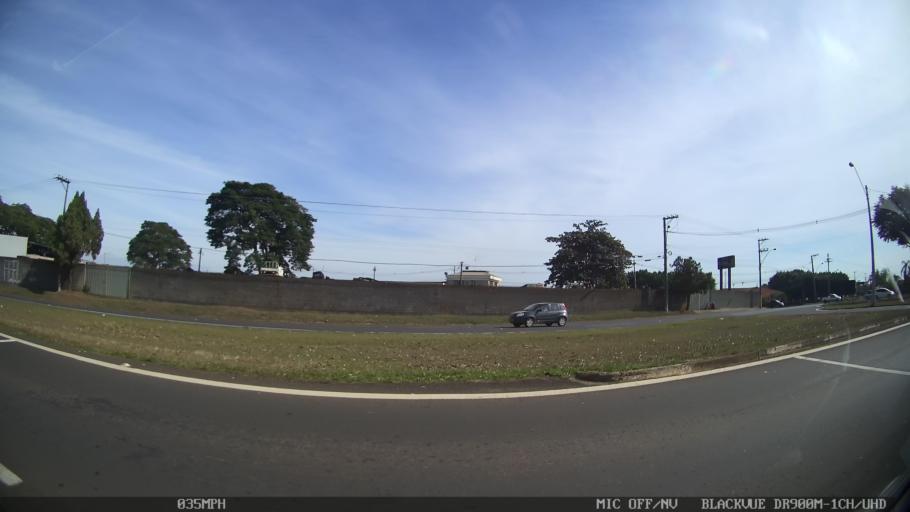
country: BR
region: Sao Paulo
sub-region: Piracicaba
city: Piracicaba
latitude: -22.7643
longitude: -47.6452
